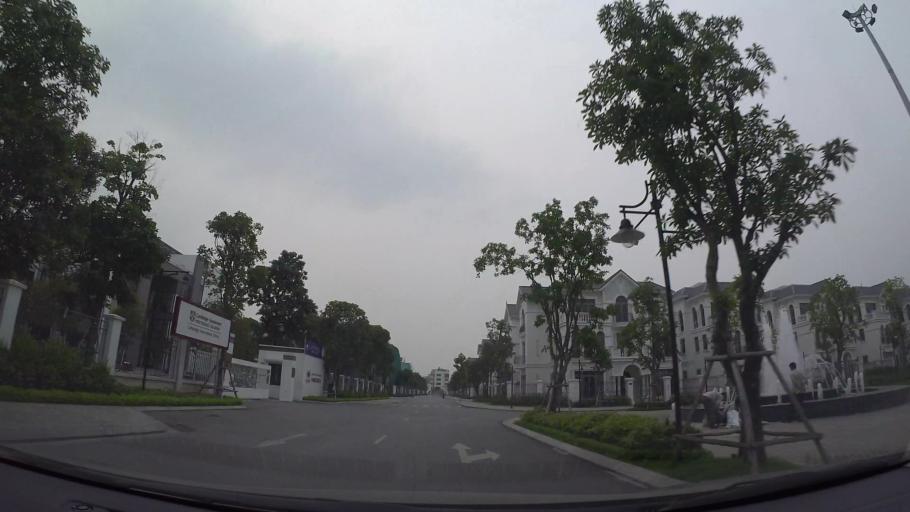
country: VN
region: Ha Noi
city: Trau Quy
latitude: 21.0485
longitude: 105.9045
